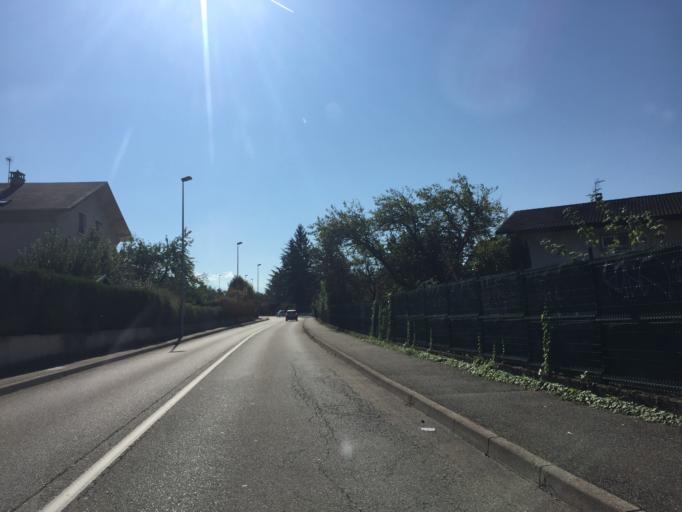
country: FR
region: Rhone-Alpes
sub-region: Departement de la Savoie
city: La Ravoire
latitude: 45.5532
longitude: 5.9677
